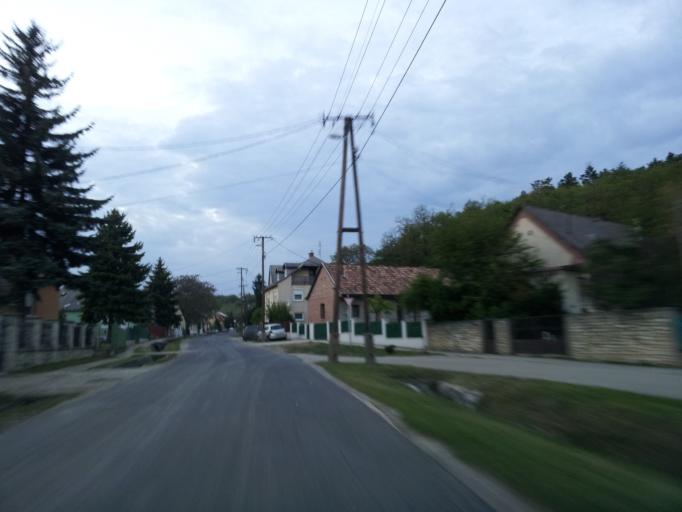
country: HU
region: Komarom-Esztergom
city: Csolnok
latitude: 47.6639
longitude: 18.7203
